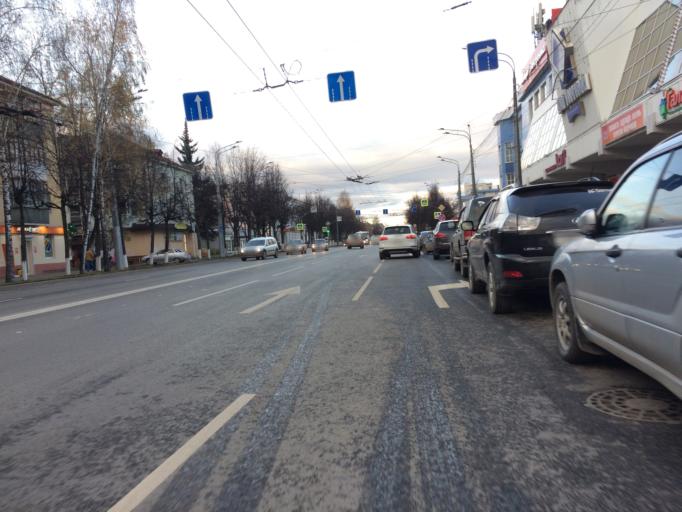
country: RU
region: Mariy-El
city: Yoshkar-Ola
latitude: 56.6338
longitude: 47.8844
